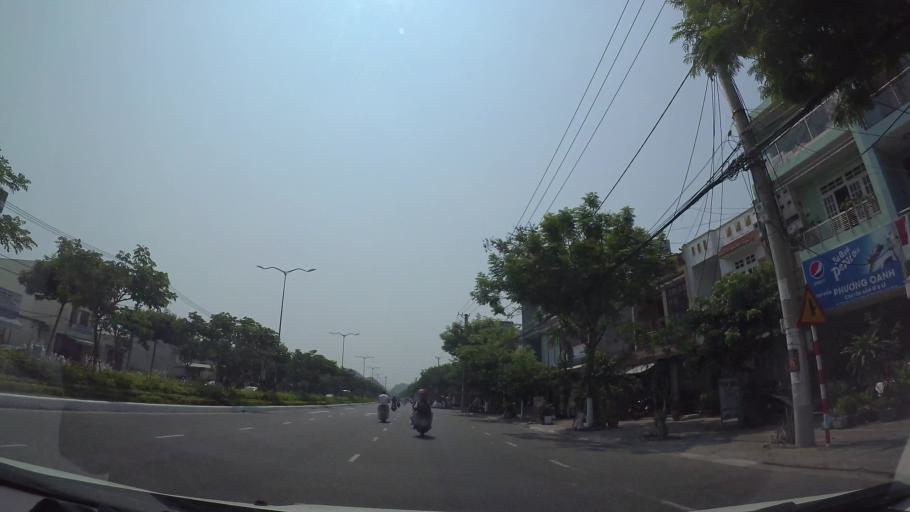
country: VN
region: Da Nang
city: Ngu Hanh Son
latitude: 16.0129
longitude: 108.2558
